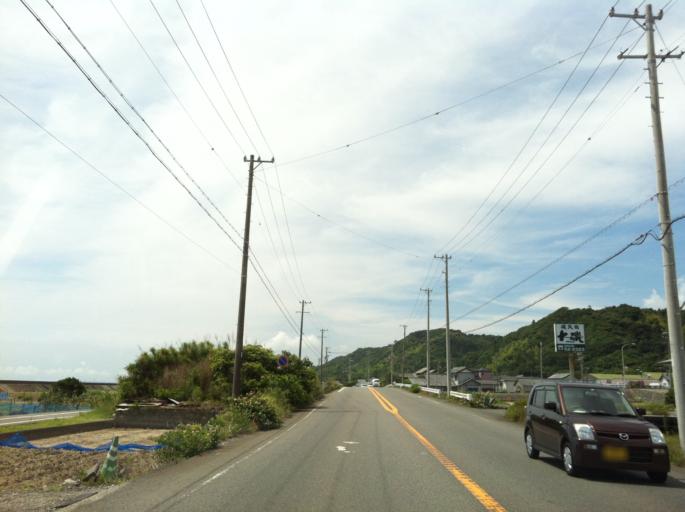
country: JP
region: Shizuoka
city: Sagara
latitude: 34.7124
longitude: 138.2143
